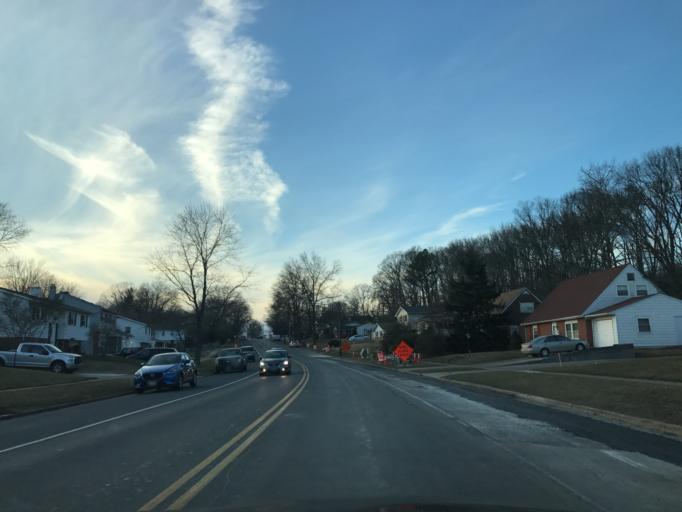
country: US
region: Maryland
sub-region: Harford County
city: Joppatowne
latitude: 39.4144
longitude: -76.3574
